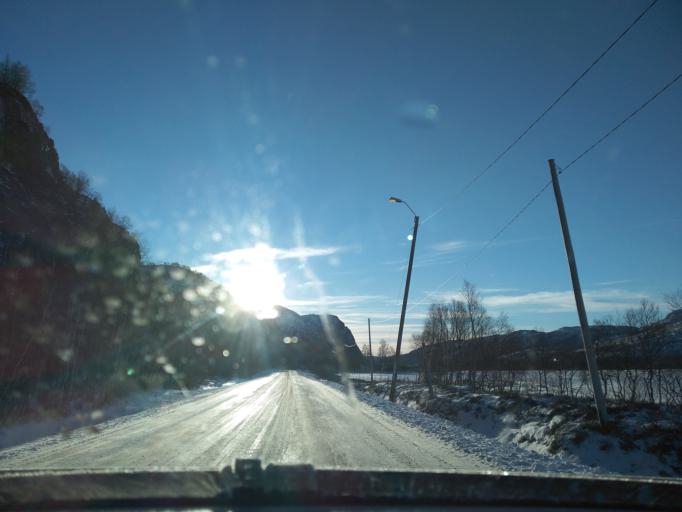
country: NO
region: Vest-Agder
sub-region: Sirdal
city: Tonstad
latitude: 59.0075
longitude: 6.9324
